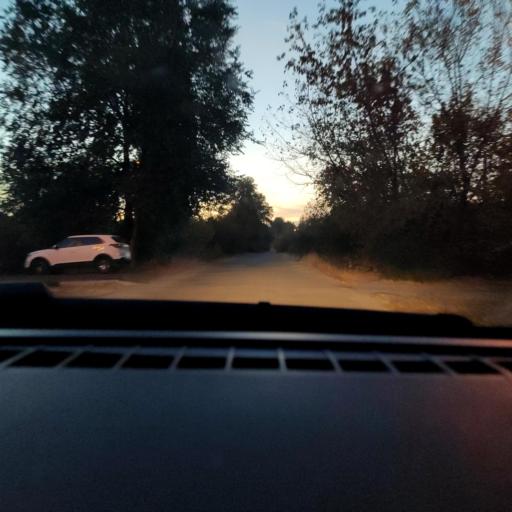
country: RU
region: Voronezj
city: Maslovka
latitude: 51.6164
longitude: 39.2626
